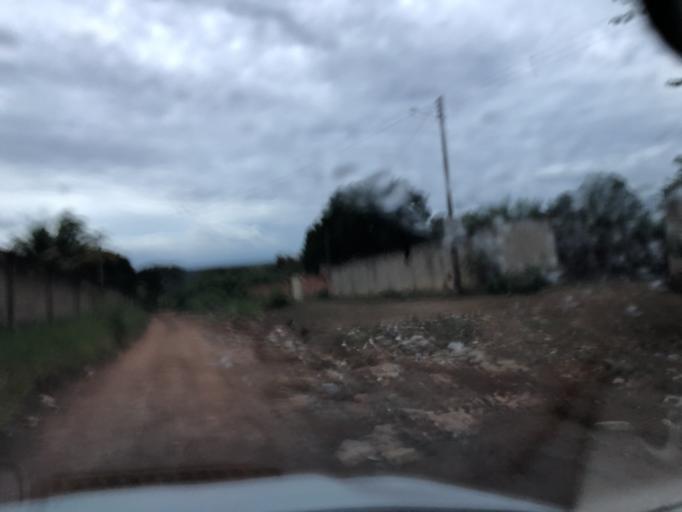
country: BR
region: Goias
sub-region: Luziania
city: Luziania
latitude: -16.1164
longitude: -47.9861
